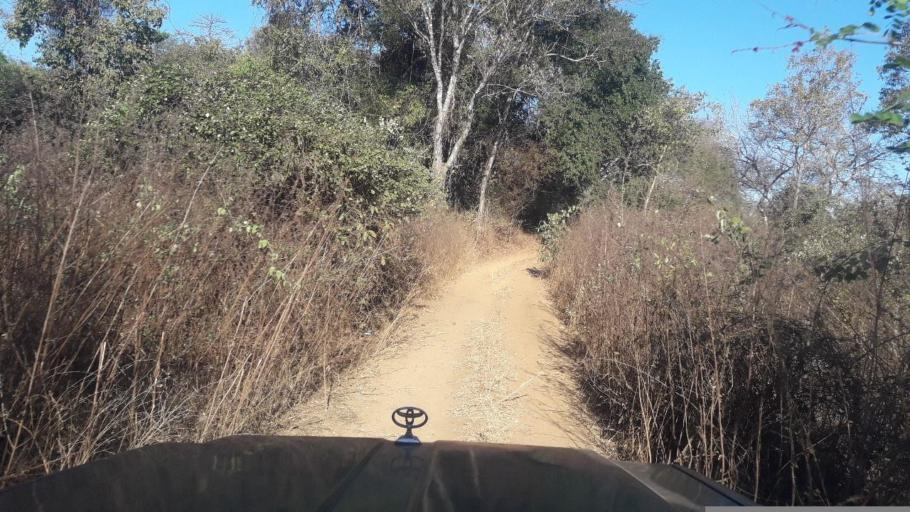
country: MG
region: Boeny
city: Sitampiky
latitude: -16.4189
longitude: 45.6139
